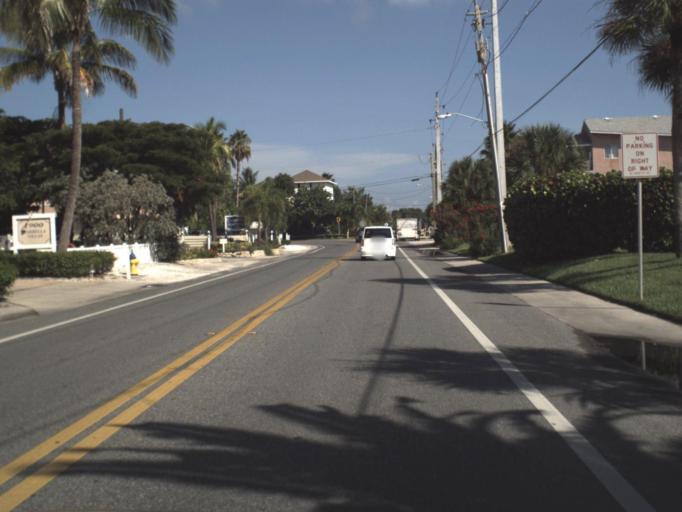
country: US
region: Florida
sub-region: Manatee County
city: Bradenton Beach
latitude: 27.4758
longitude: -82.7022
